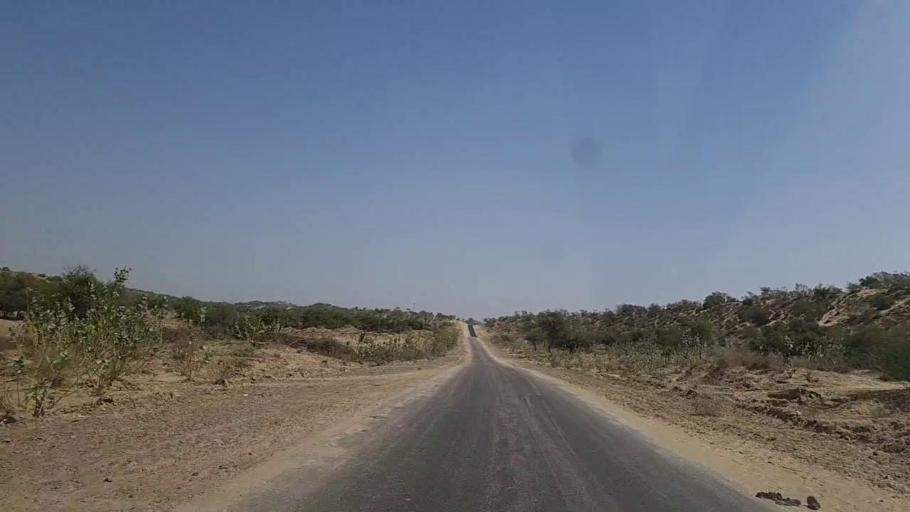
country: PK
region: Sindh
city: Diplo
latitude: 24.4809
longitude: 69.4882
